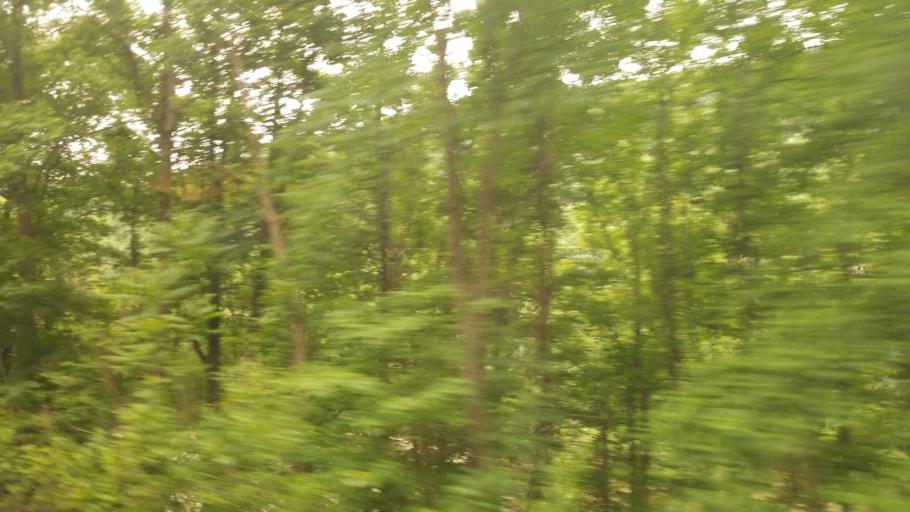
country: US
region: Pennsylvania
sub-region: Fayette County
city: South Connellsville
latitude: 39.9311
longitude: -79.4869
